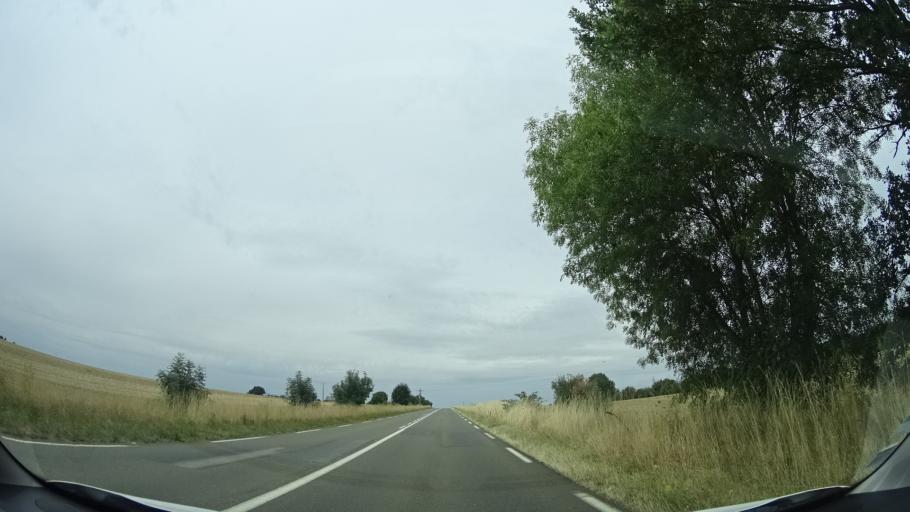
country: FR
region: Pays de la Loire
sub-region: Departement de la Mayenne
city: Meslay-du-Maine
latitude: 47.9271
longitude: -0.4891
